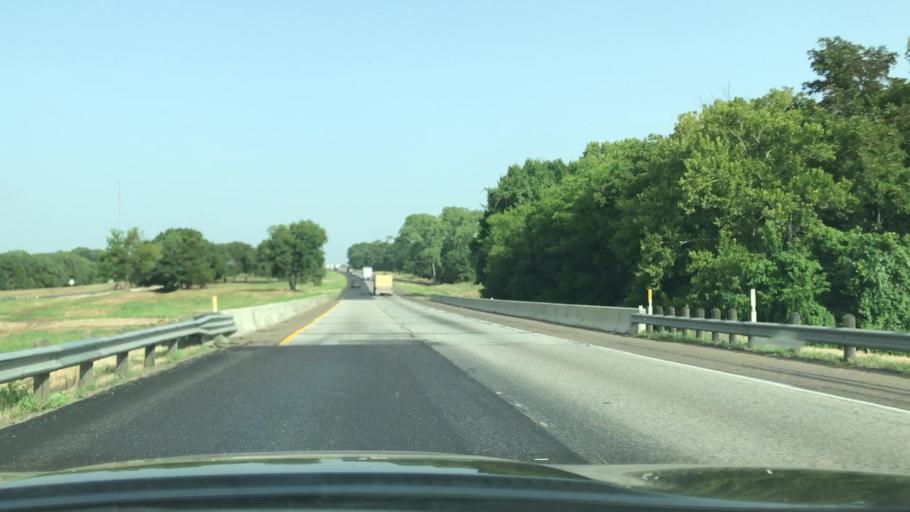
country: US
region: Texas
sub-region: Van Zandt County
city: Wills Point
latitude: 32.6612
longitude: -96.1156
